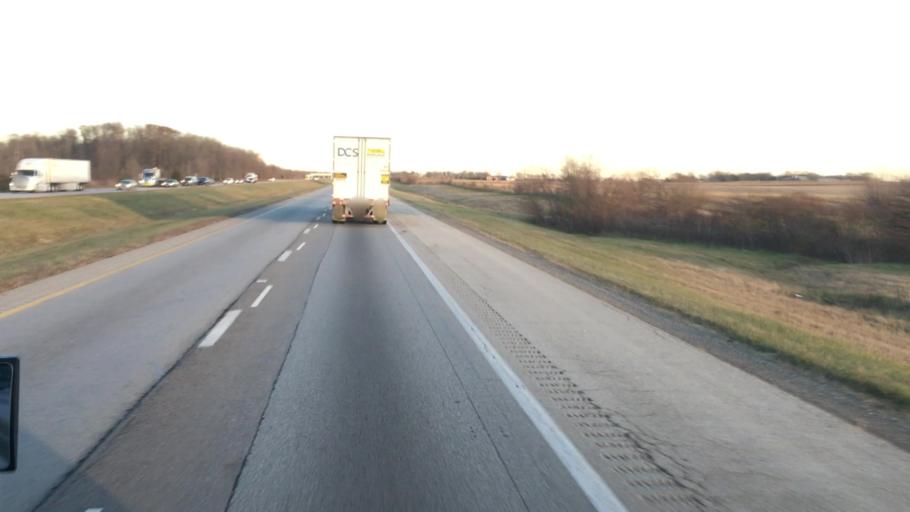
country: US
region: Ohio
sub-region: Preble County
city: Lewisburg
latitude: 39.8376
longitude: -84.4994
